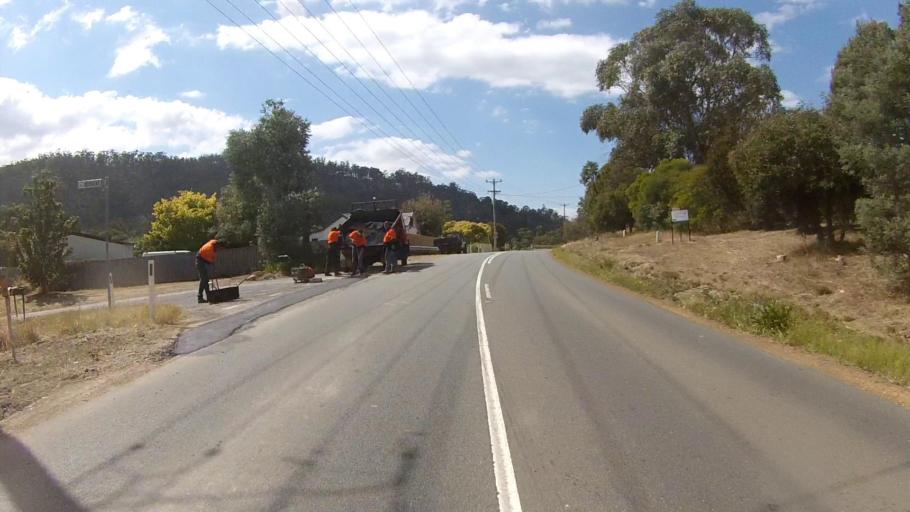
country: AU
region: Tasmania
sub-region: Clarence
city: Cambridge
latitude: -42.8393
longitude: 147.4247
